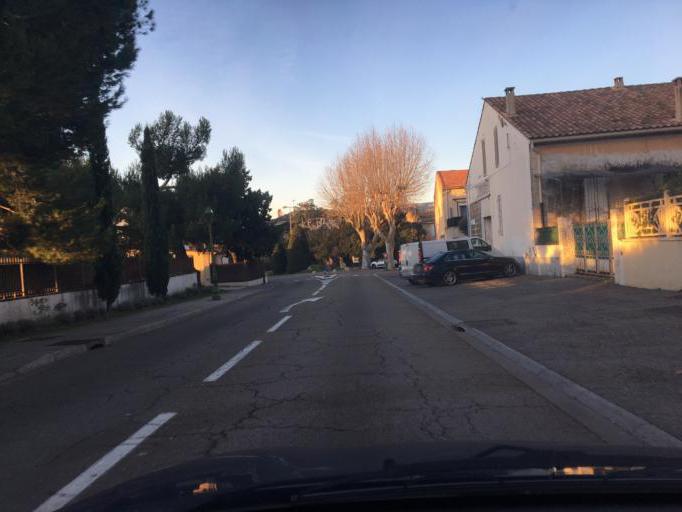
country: FR
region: Provence-Alpes-Cote d'Azur
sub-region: Departement des Bouches-du-Rhone
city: Mallemort
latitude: 43.7309
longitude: 5.1773
